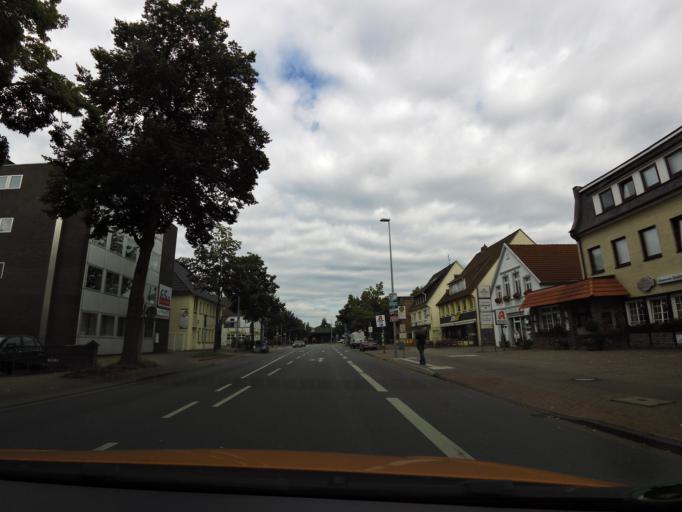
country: DE
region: Lower Saxony
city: Oldenburg
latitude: 53.1429
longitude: 8.1943
